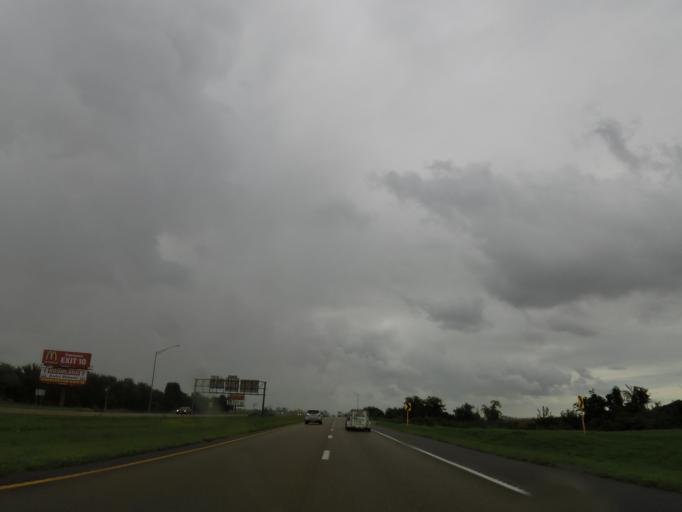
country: US
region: Missouri
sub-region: Scott County
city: Sikeston
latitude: 36.8748
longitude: -89.5298
